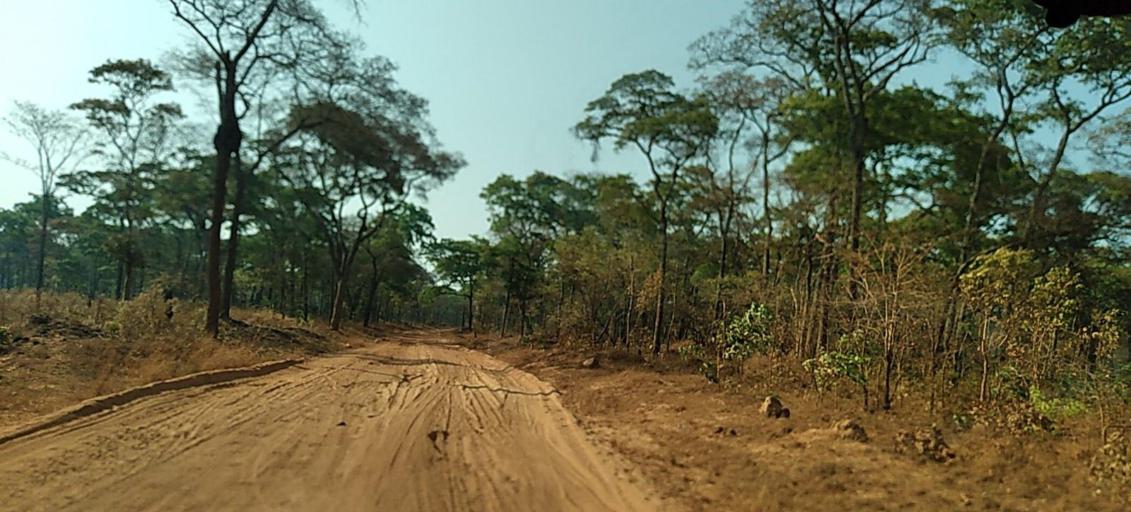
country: ZM
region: North-Western
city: Kasempa
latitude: -13.6282
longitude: 25.9863
